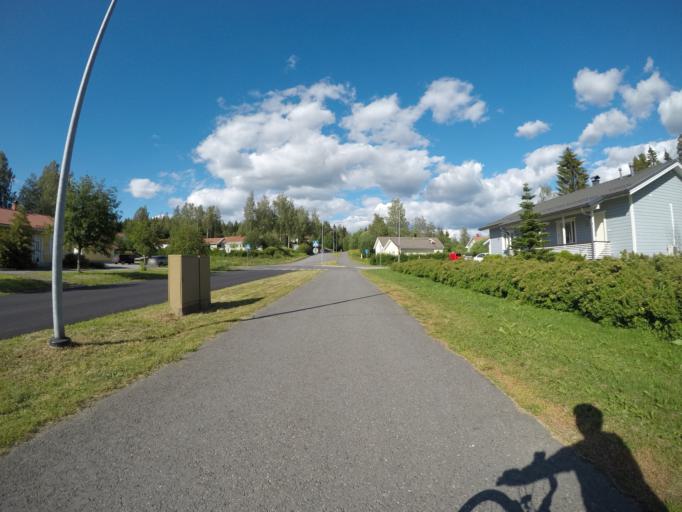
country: FI
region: Haeme
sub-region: Haemeenlinna
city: Haemeenlinna
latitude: 61.0205
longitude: 24.5194
